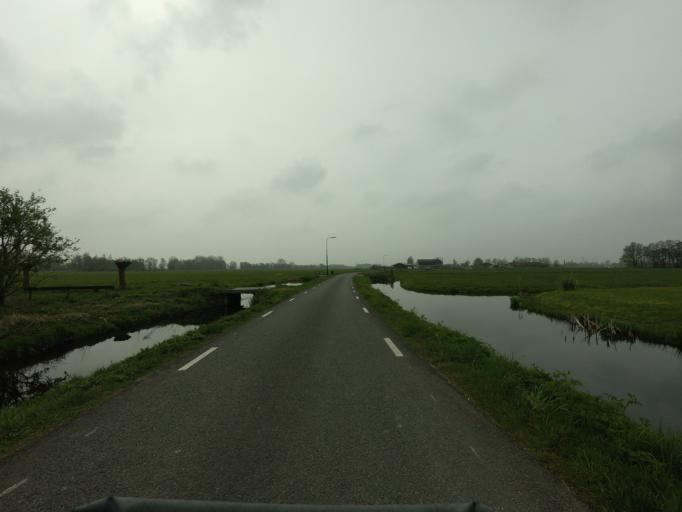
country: NL
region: South Holland
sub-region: Molenwaard
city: Nieuw-Lekkerland
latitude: 51.9254
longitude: 4.6732
